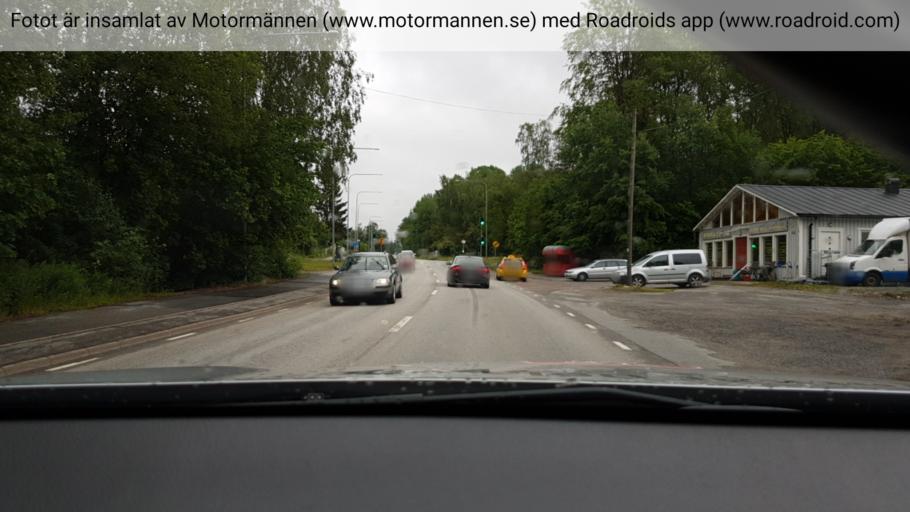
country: SE
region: Stockholm
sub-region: Huddinge Kommun
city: Huddinge
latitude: 59.2277
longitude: 17.9641
